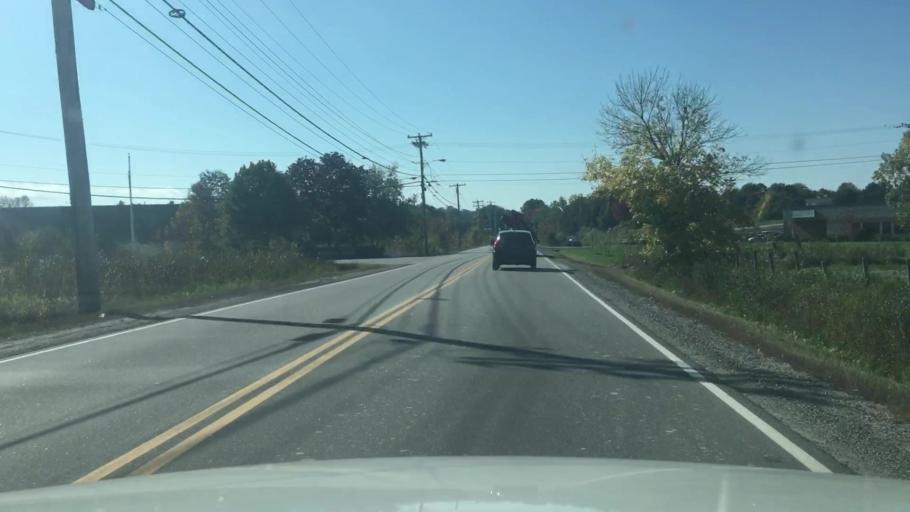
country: US
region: Maine
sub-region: Cumberland County
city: Westbrook
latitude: 43.6501
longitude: -70.3639
